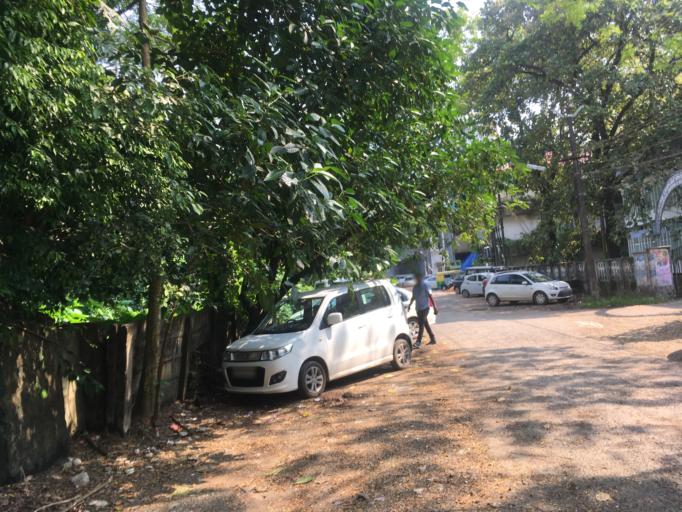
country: IN
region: Kerala
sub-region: Ernakulam
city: Cochin
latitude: 9.9873
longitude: 76.2733
